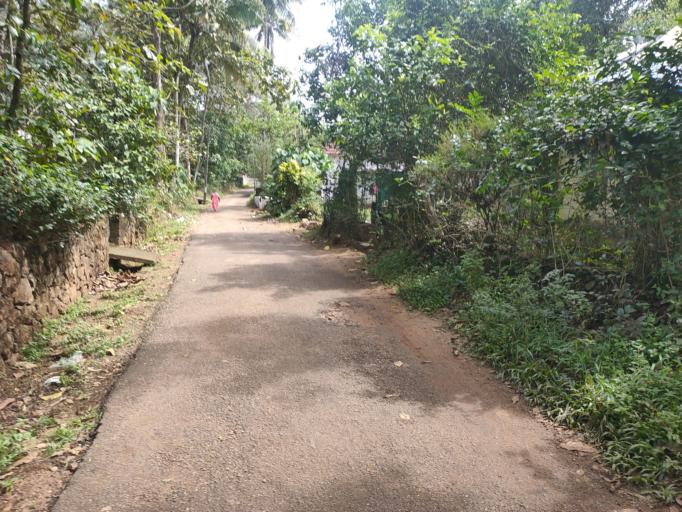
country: IN
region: Kerala
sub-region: Ernakulam
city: Kotamangalam
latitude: 10.0053
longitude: 76.6423
